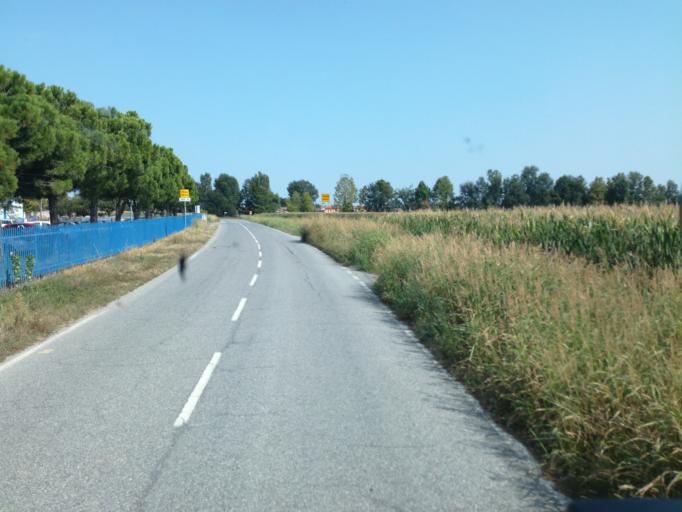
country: IT
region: Lombardy
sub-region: Provincia di Brescia
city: Dello
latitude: 45.4181
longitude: 10.0874
